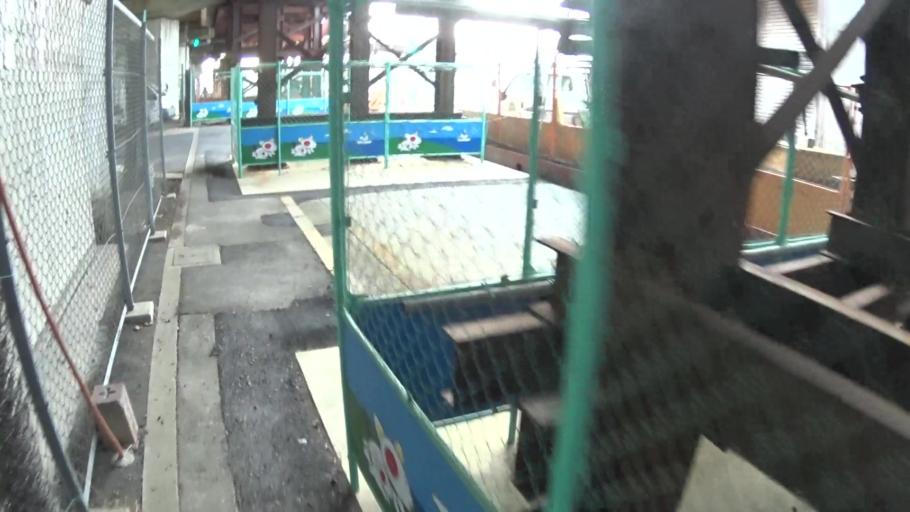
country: JP
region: Tokyo
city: Mitaka-shi
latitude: 35.6743
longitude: 139.5833
